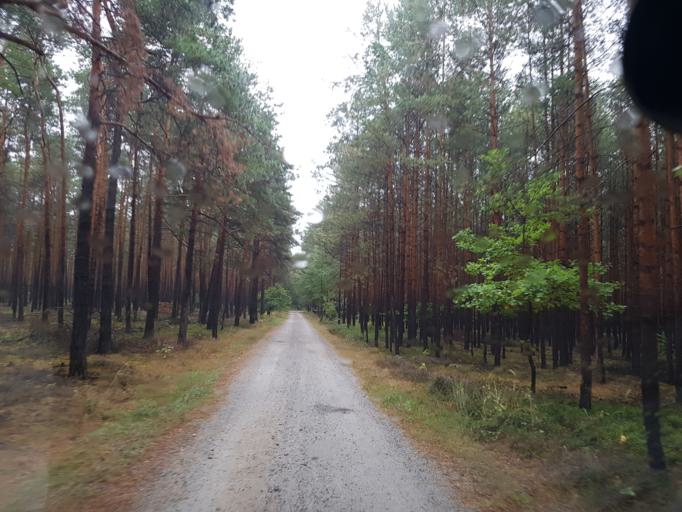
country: DE
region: Brandenburg
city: Finsterwalde
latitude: 51.6147
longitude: 13.7776
